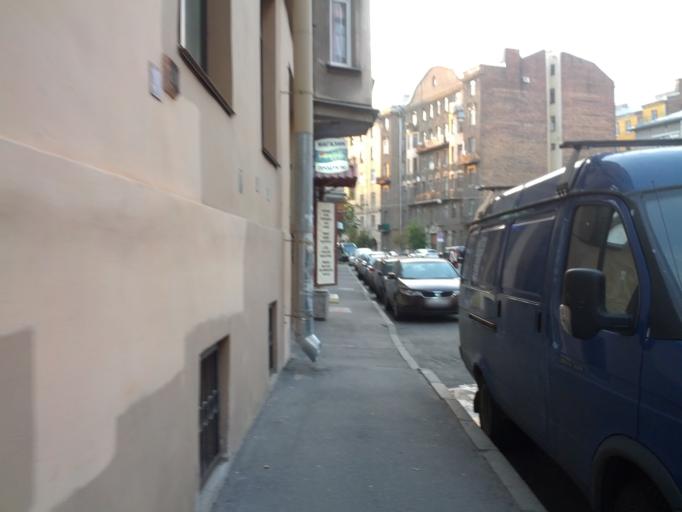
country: RU
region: St.-Petersburg
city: Petrogradka
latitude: 59.9539
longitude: 30.3024
